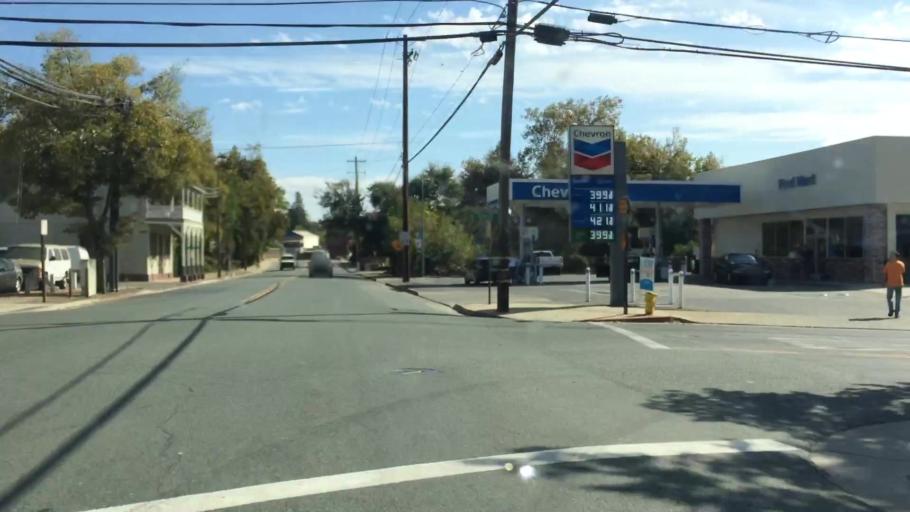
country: US
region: California
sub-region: Amador County
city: Ione
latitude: 38.3542
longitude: -120.9359
